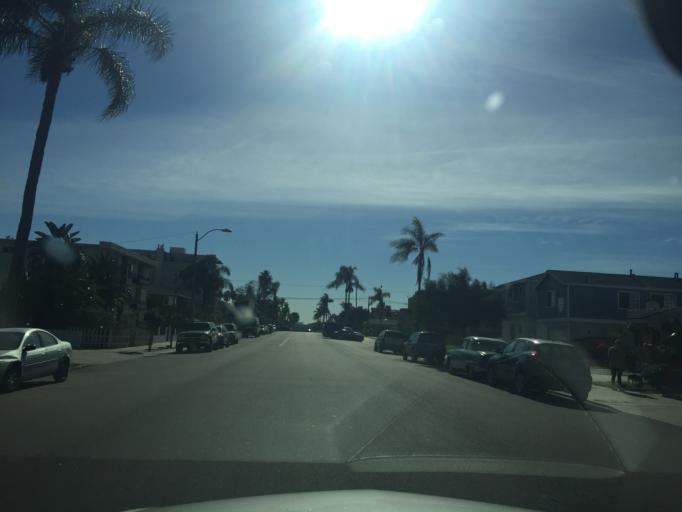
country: US
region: California
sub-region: San Diego County
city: San Diego
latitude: 32.7534
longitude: -117.1277
